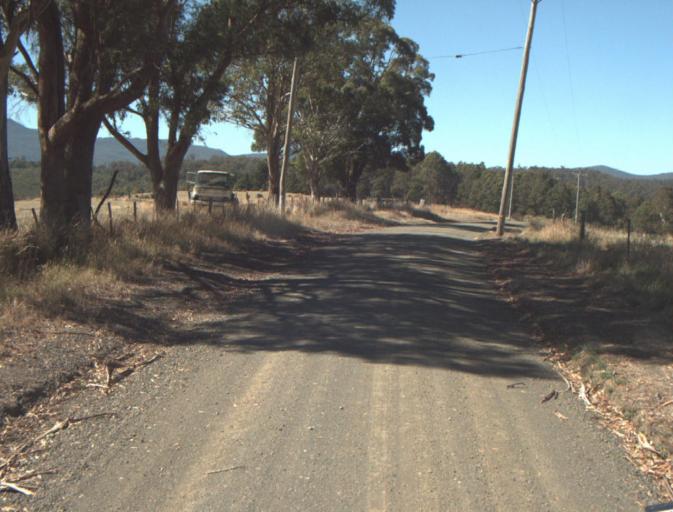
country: AU
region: Tasmania
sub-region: Launceston
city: Newstead
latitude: -41.3109
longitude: 147.3209
